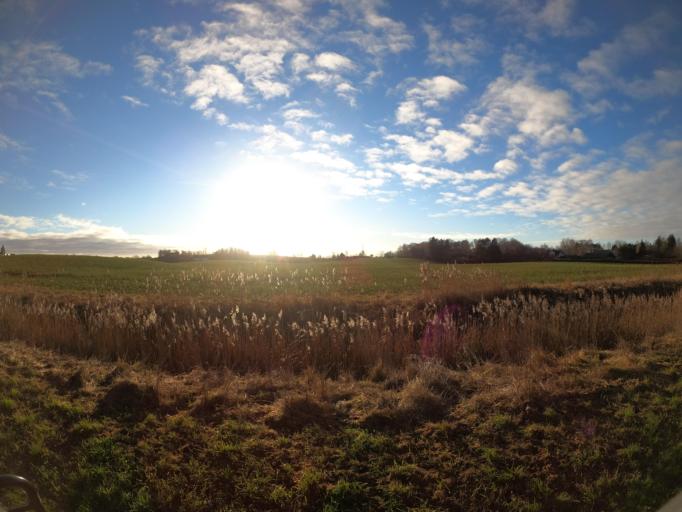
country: SE
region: Skane
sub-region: Svedala Kommun
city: Svedala
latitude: 55.5048
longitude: 13.2298
